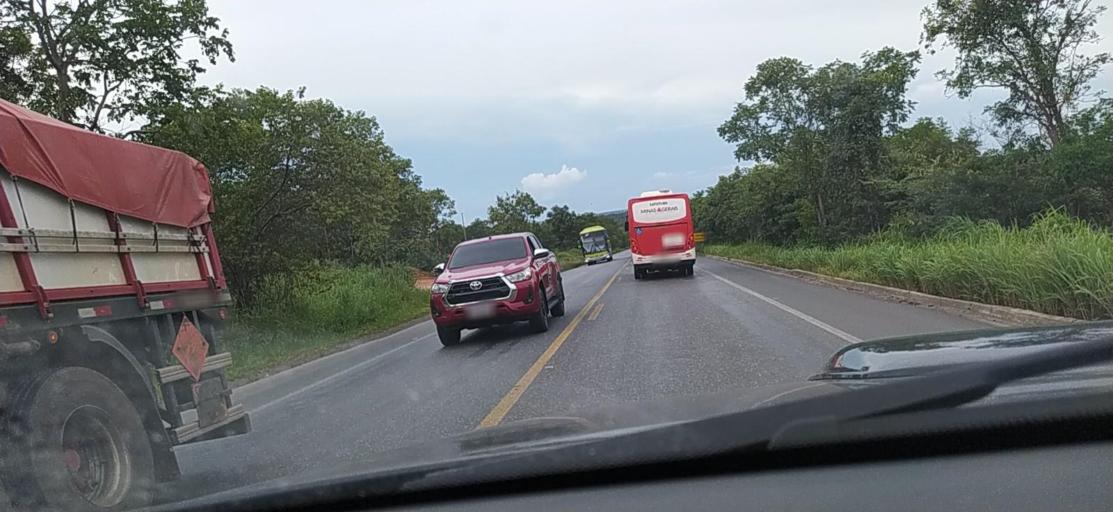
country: BR
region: Minas Gerais
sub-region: Montes Claros
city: Montes Claros
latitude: -16.6680
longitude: -43.7887
